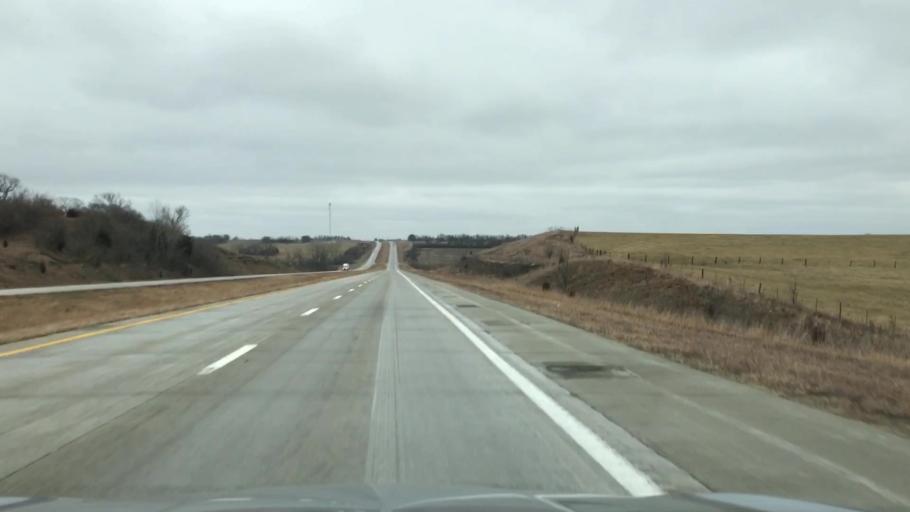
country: US
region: Missouri
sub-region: Caldwell County
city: Hamilton
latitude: 39.7348
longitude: -93.7883
